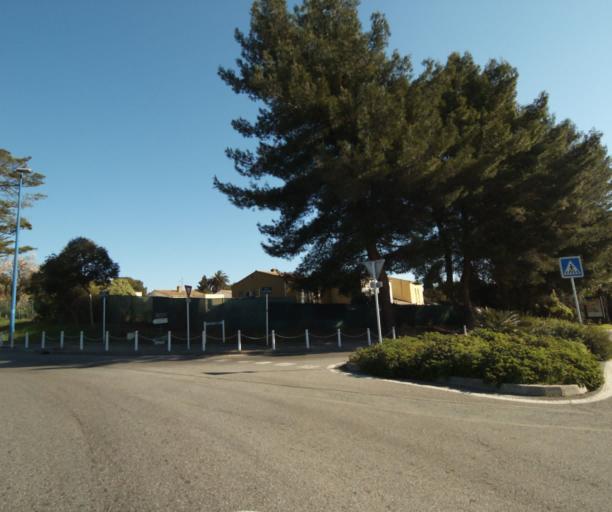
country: FR
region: Provence-Alpes-Cote d'Azur
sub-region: Departement des Alpes-Maritimes
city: Biot
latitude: 43.6021
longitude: 7.0916
